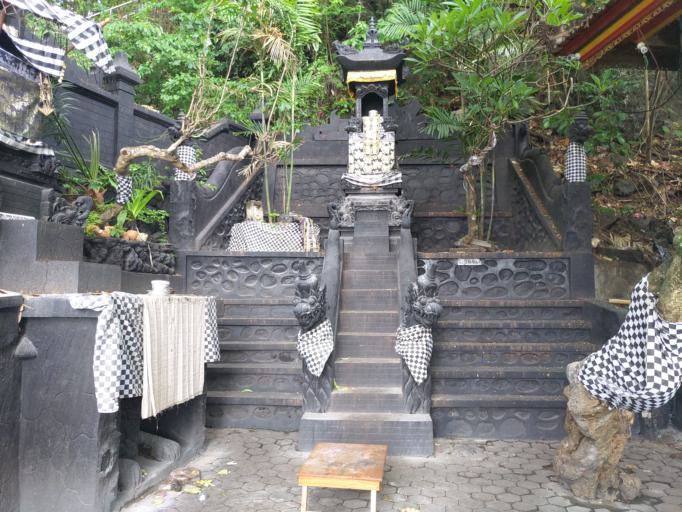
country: ID
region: West Nusa Tenggara
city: Mambalan
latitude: -8.5089
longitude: 116.0569
